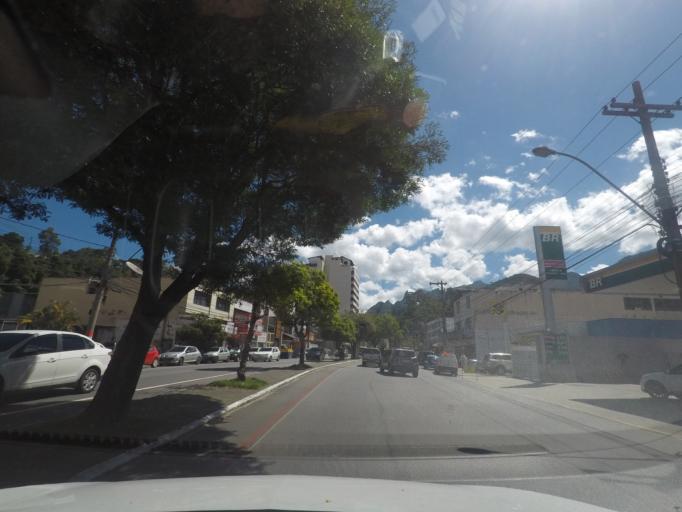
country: BR
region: Rio de Janeiro
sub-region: Teresopolis
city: Teresopolis
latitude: -22.4219
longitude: -42.9762
